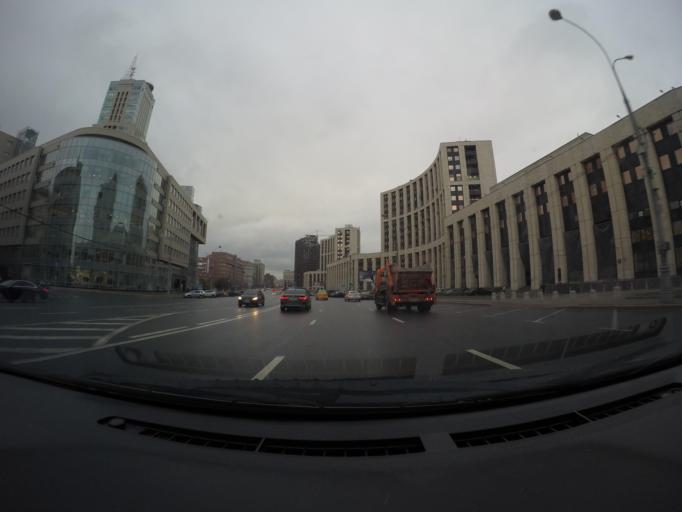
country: RU
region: Moscow
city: Sokol'niki
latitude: 55.7737
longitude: 37.6486
